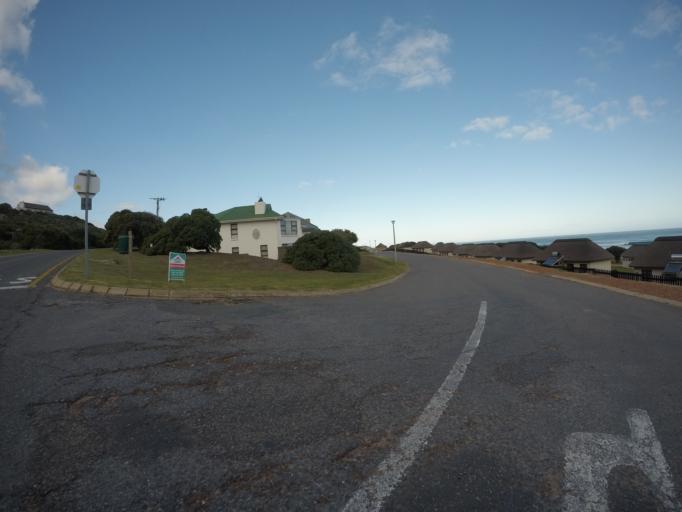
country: ZA
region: Western Cape
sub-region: Eden District Municipality
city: Riversdale
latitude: -34.4244
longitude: 21.3387
